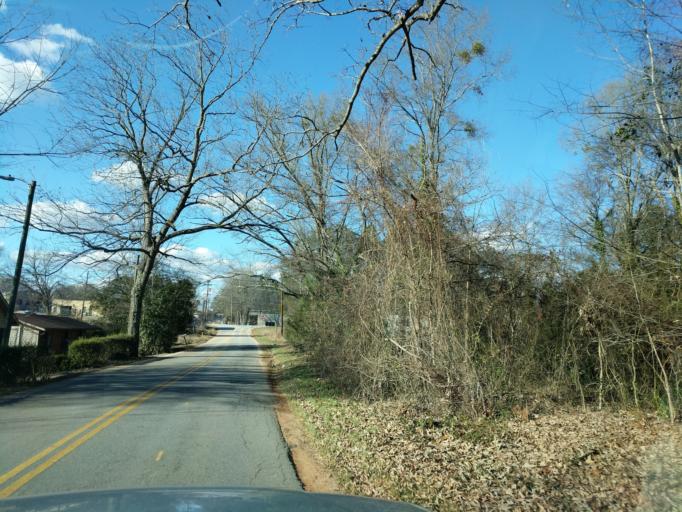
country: US
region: South Carolina
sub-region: Greenwood County
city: Greenwood
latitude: 34.2080
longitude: -82.1418
